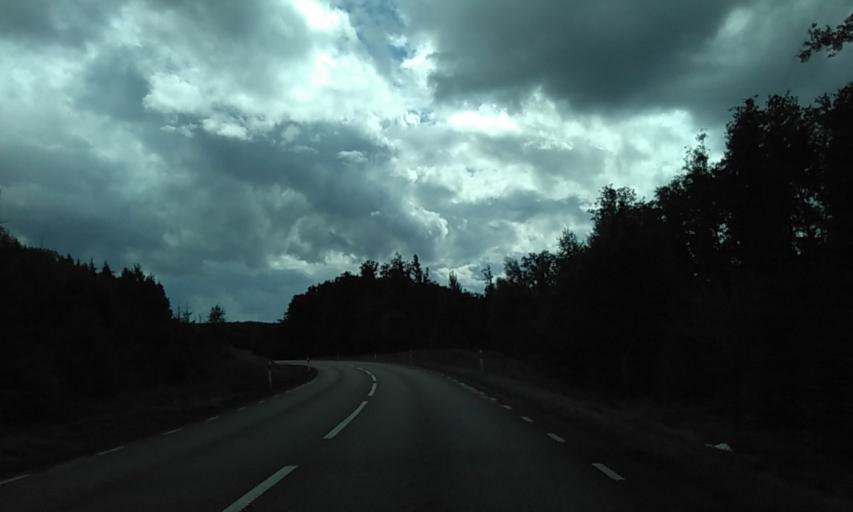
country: SE
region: Vaestra Goetaland
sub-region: Alingsas Kommun
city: Alingsas
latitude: 57.9641
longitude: 12.4444
